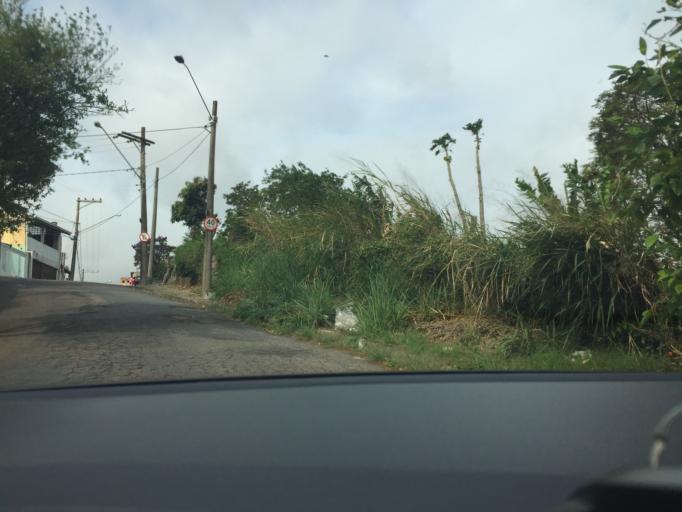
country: BR
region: Sao Paulo
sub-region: Jundiai
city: Jundiai
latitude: -23.2056
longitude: -46.8976
